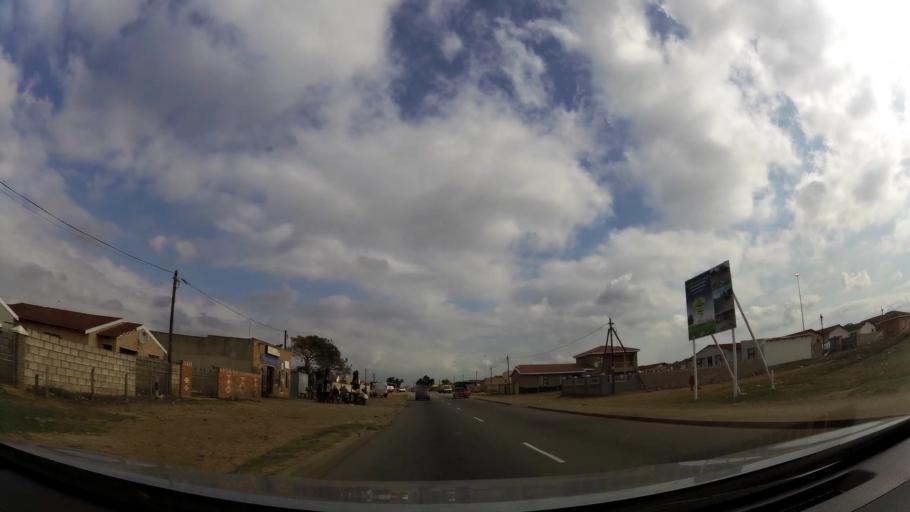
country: ZA
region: Eastern Cape
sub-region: Nelson Mandela Bay Metropolitan Municipality
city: Port Elizabeth
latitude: -33.8155
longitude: 25.5865
